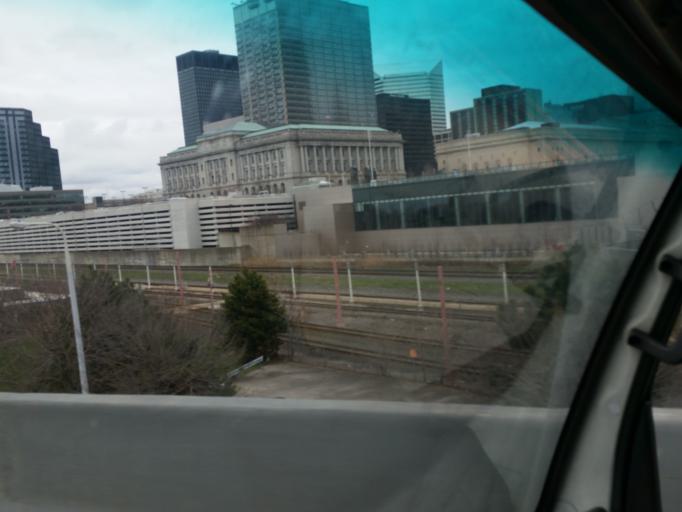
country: US
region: Ohio
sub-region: Cuyahoga County
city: Cleveland
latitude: 41.5054
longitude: -81.6976
